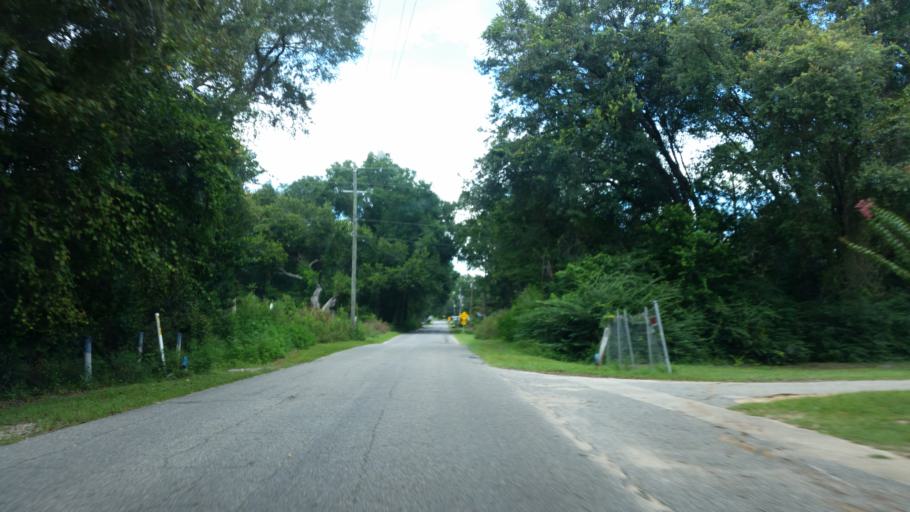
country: US
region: Florida
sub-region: Escambia County
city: Ensley
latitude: 30.5440
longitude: -87.2663
